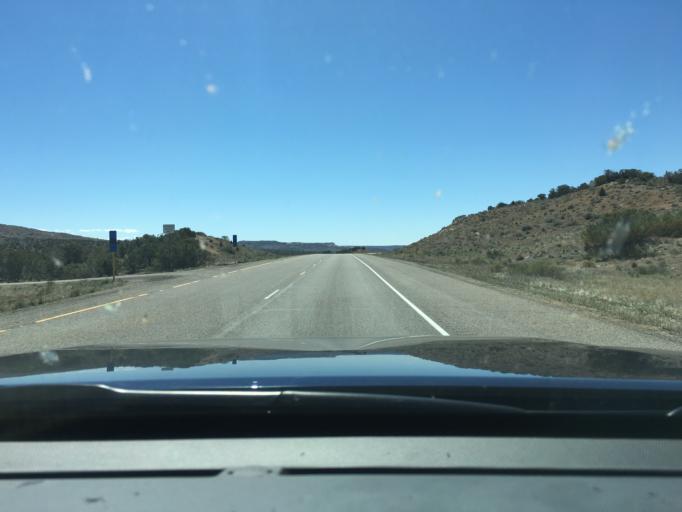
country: US
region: Colorado
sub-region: Mesa County
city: Loma
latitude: 39.2150
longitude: -108.9649
